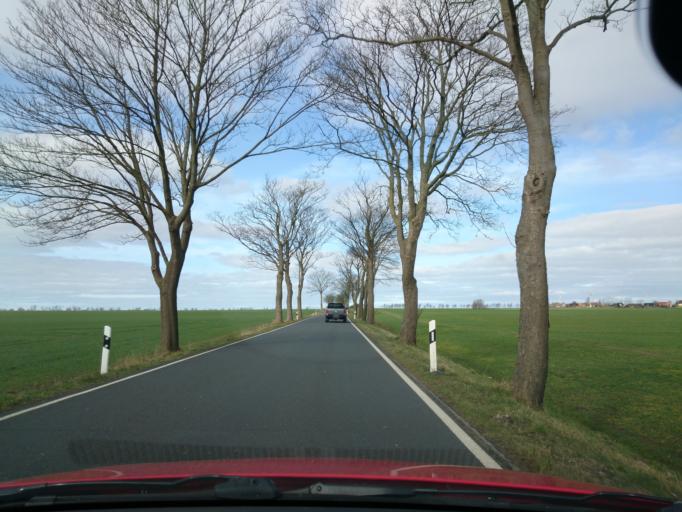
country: DE
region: Mecklenburg-Vorpommern
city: Barth
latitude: 54.3444
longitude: 12.7763
